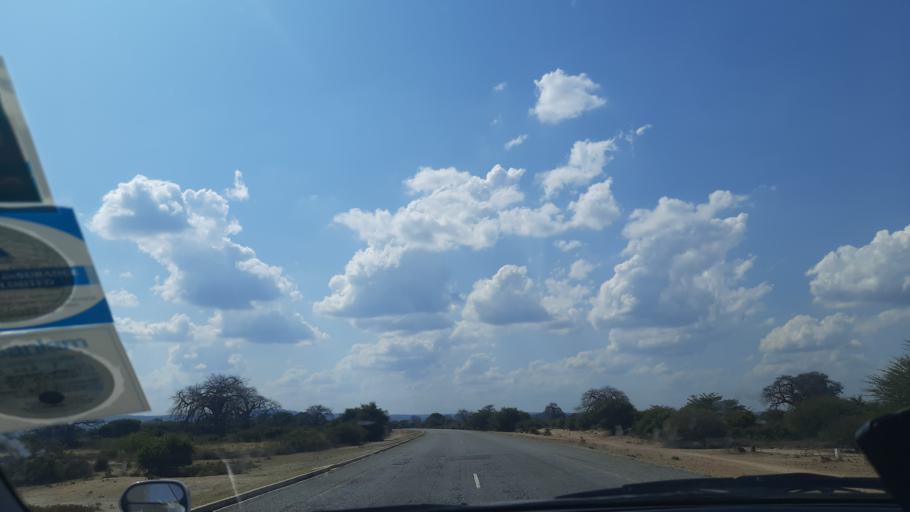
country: TZ
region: Singida
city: Kilimatinde
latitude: -5.8393
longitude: 35.0647
